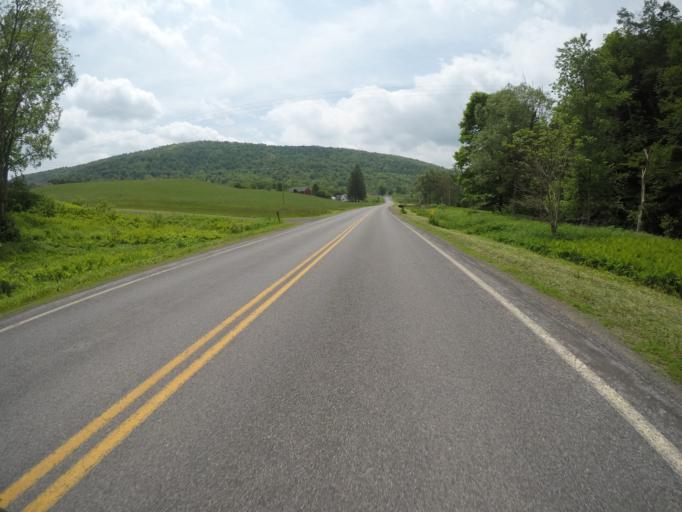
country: US
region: New York
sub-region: Delaware County
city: Delhi
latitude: 42.2487
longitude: -74.8086
